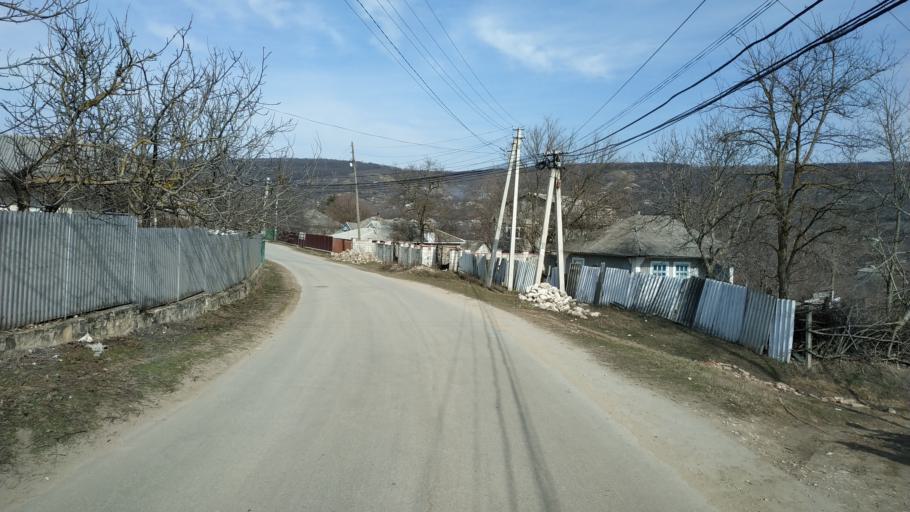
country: MD
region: Nisporeni
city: Nisporeni
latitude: 47.2024
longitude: 28.0647
